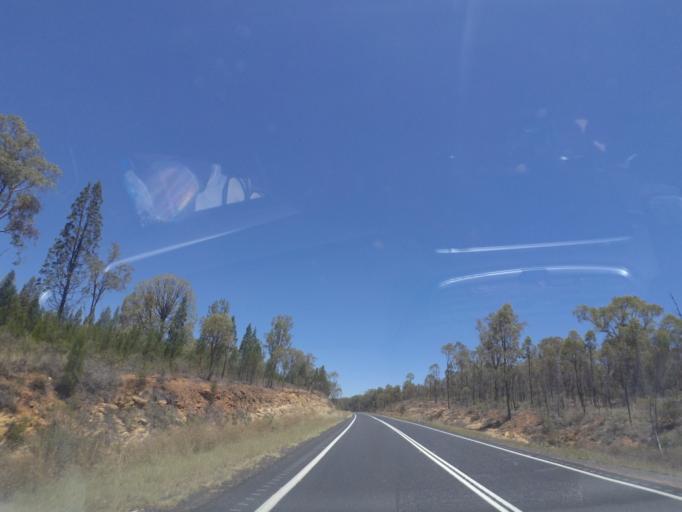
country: AU
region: New South Wales
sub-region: Warrumbungle Shire
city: Coonabarabran
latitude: -31.1803
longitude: 149.3557
